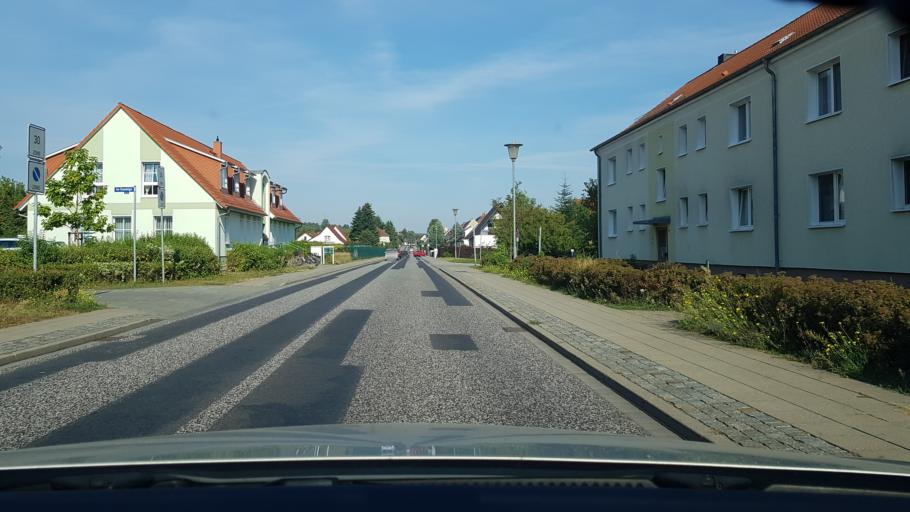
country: DE
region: Brandenburg
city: Eisenhuettenstadt
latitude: 52.1482
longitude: 14.6162
